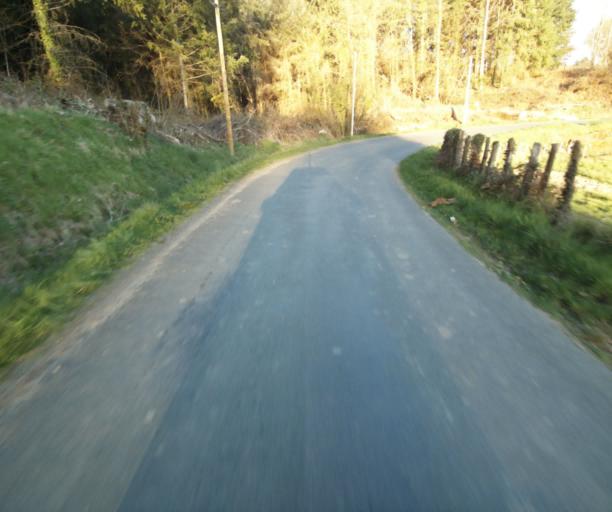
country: FR
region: Limousin
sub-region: Departement de la Correze
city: Saint-Clement
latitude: 45.3373
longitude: 1.7109
